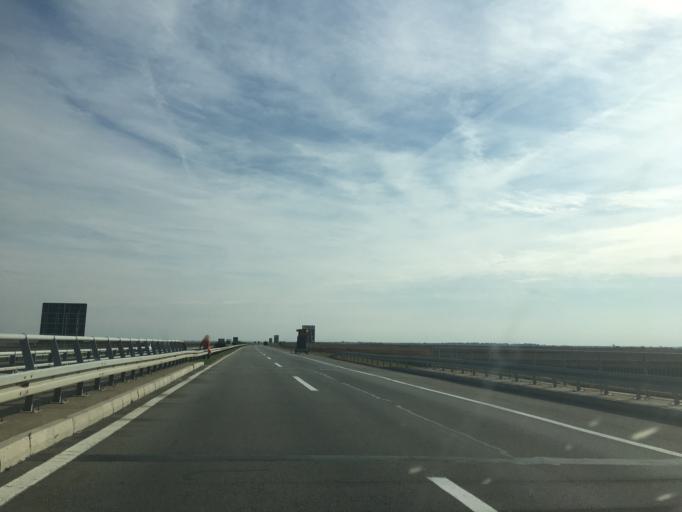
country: RS
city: Novi Karlovci
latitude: 45.0653
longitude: 20.1576
